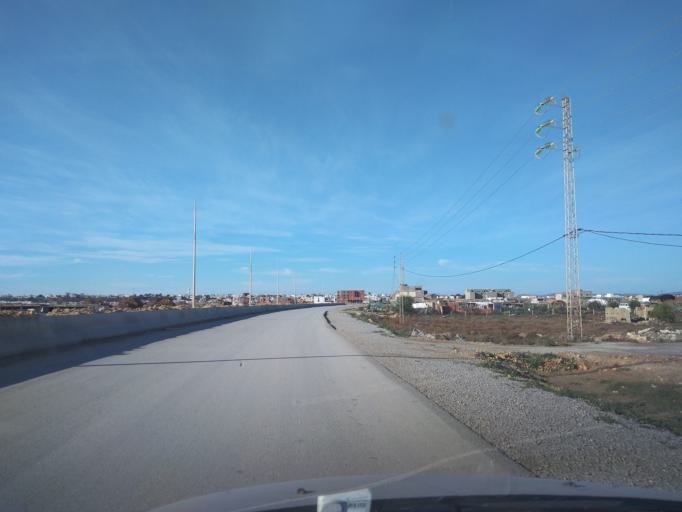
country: TN
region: Ariana
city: Qal'at al Andalus
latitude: 37.0467
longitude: 10.1254
